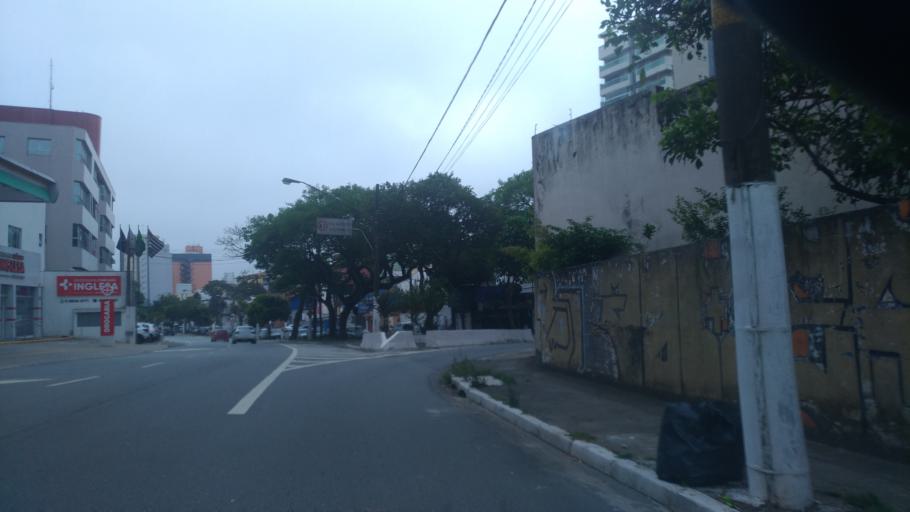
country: BR
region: Sao Paulo
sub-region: Sao Bernardo Do Campo
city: Sao Bernardo do Campo
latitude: -23.6962
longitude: -46.5611
